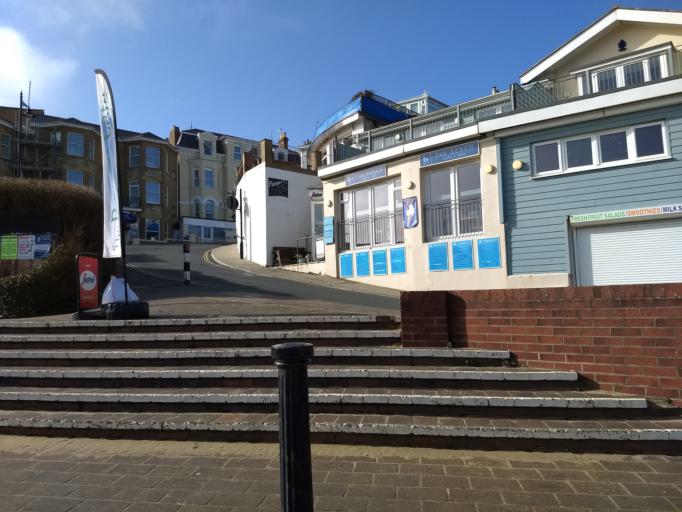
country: GB
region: England
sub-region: Isle of Wight
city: Sandown
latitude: 50.6531
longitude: -1.1551
